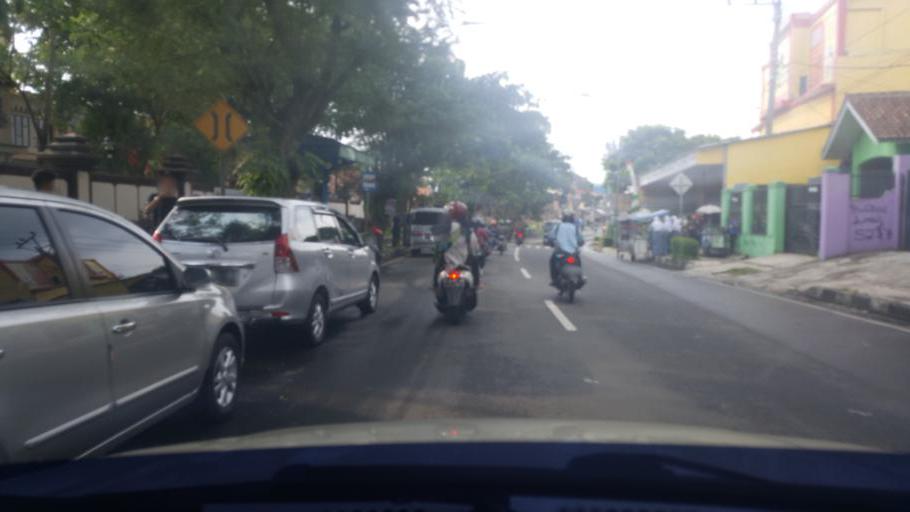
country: ID
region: West Java
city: Jati
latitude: -7.3022
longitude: 108.2035
